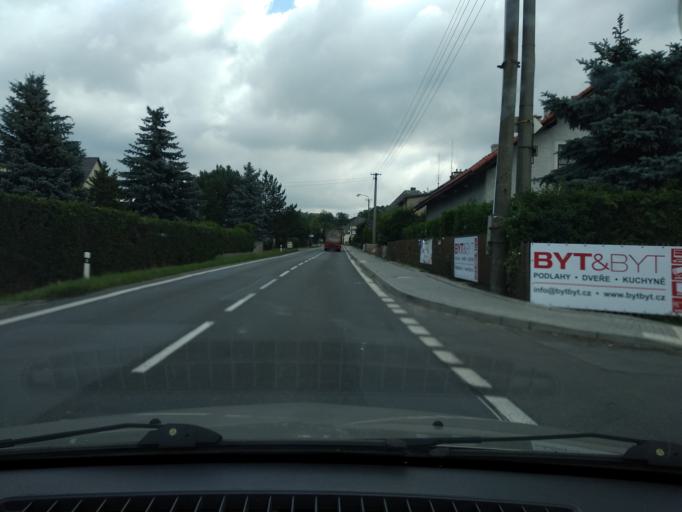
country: CZ
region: Olomoucky
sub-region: Okres Sumperk
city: Bludov
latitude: 49.9341
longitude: 16.9274
